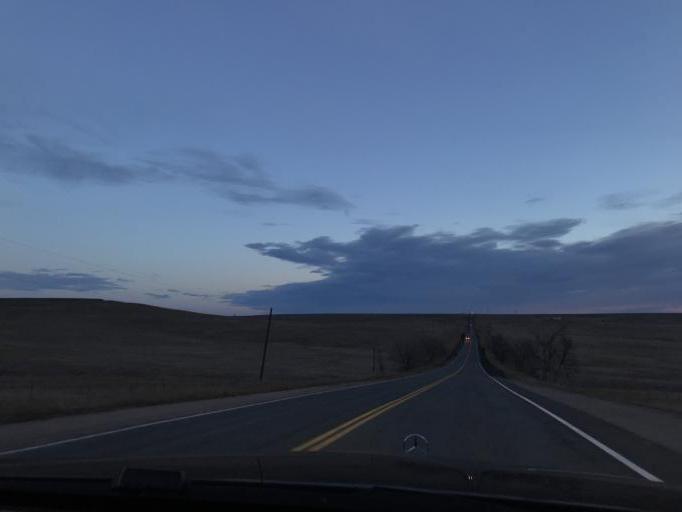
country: US
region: Colorado
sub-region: Boulder County
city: Superior
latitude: 39.8923
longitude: -105.1655
